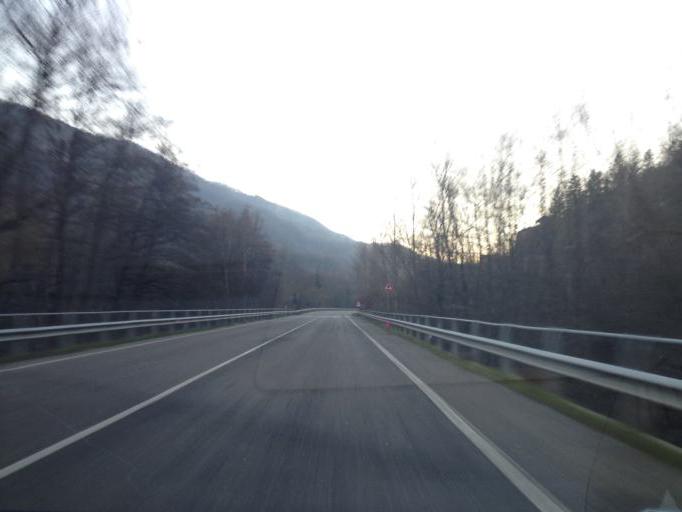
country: IT
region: The Marches
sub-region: Provincia di Ascoli Piceno
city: Arquata del Tronto
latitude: 42.7620
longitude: 13.2856
